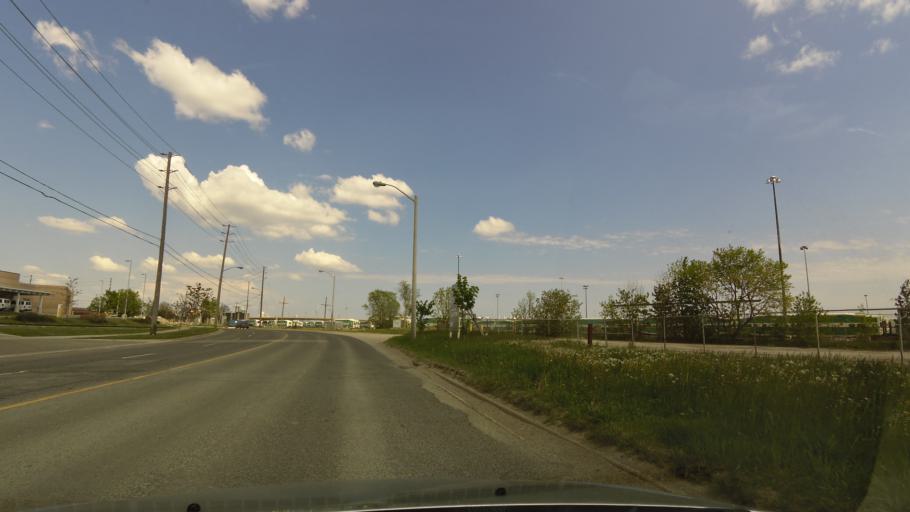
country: CA
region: Ontario
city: Etobicoke
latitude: 43.6080
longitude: -79.5165
